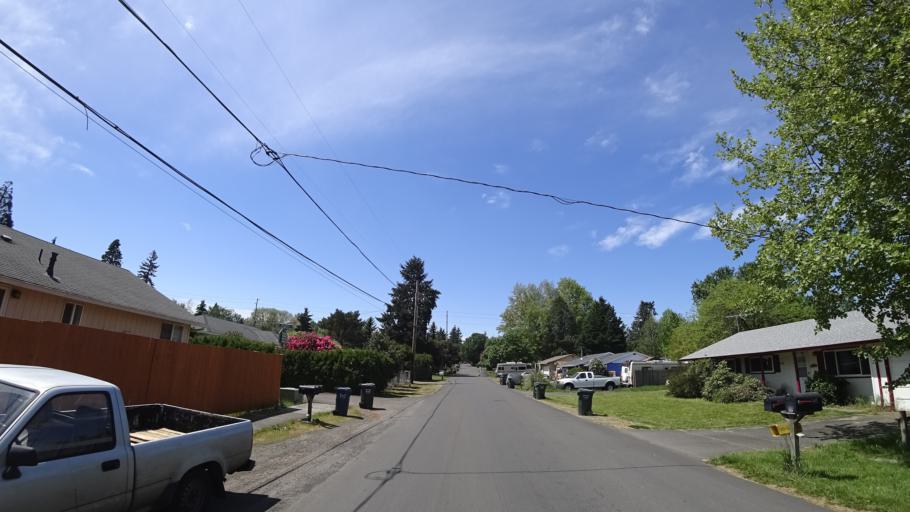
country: US
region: Oregon
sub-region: Washington County
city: Aloha
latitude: 45.4869
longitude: -122.8533
